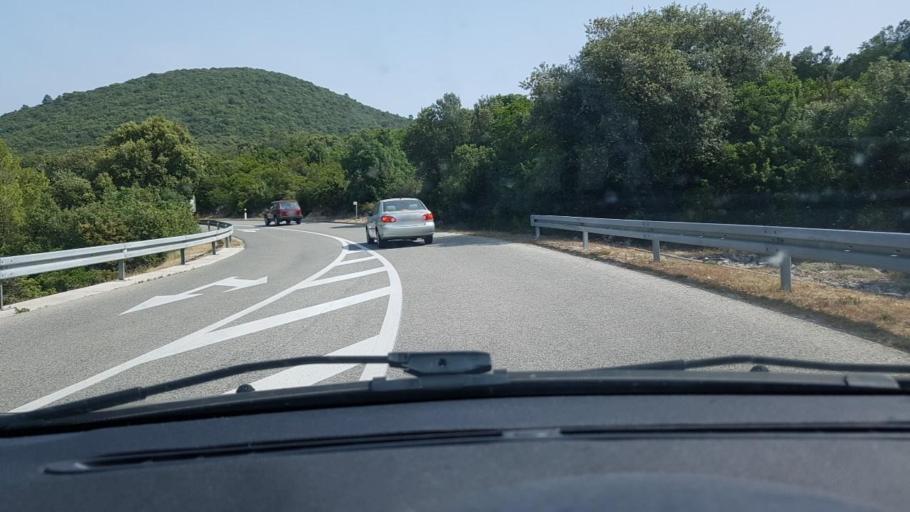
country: HR
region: Dubrovacko-Neretvanska
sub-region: Grad Korcula
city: Zrnovo
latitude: 42.9421
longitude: 17.0534
